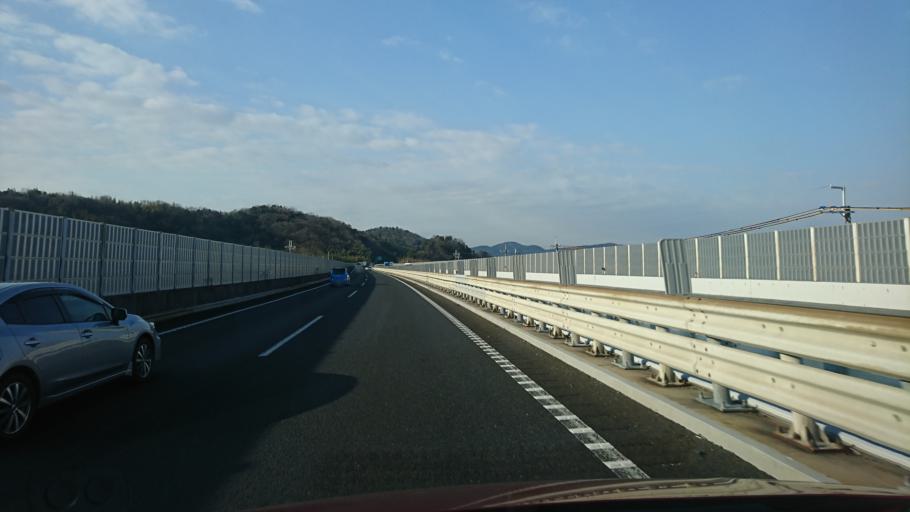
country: JP
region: Hyogo
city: Tatsunocho-tominaga
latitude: 34.8507
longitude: 134.5334
